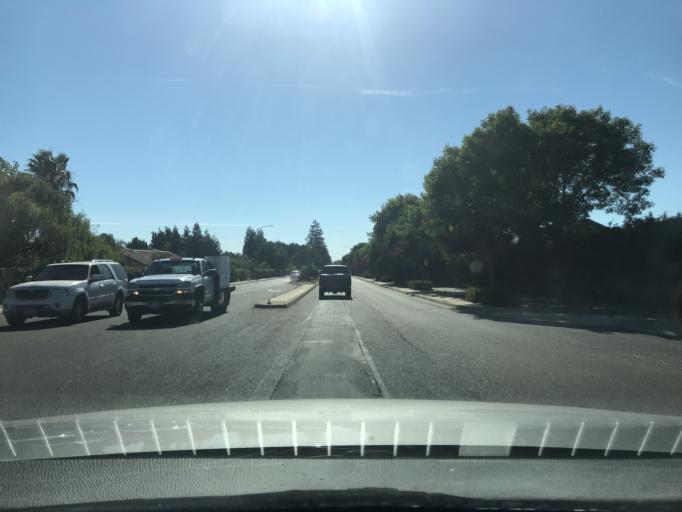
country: US
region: California
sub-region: Merced County
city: Atwater
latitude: 37.3497
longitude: -120.5809
